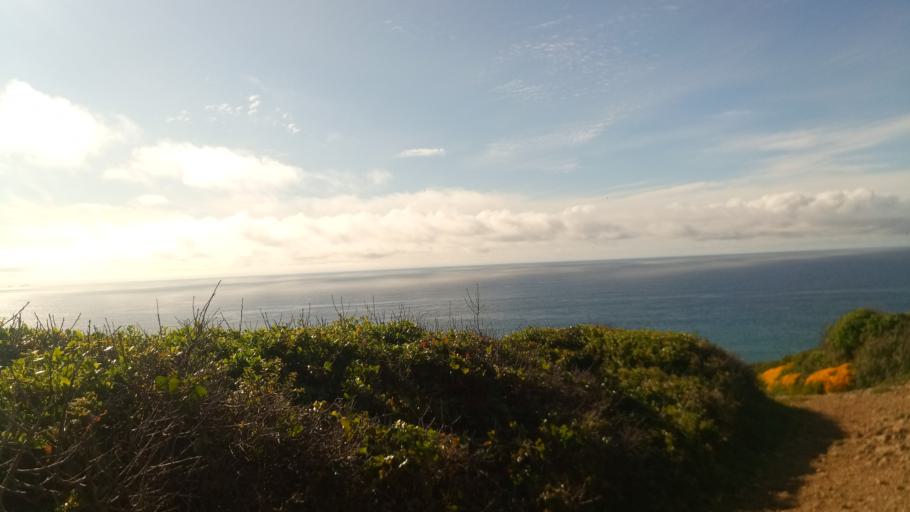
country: PT
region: Leiria
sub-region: Caldas da Rainha
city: Caldas da Rainha
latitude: 39.4935
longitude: -9.1737
